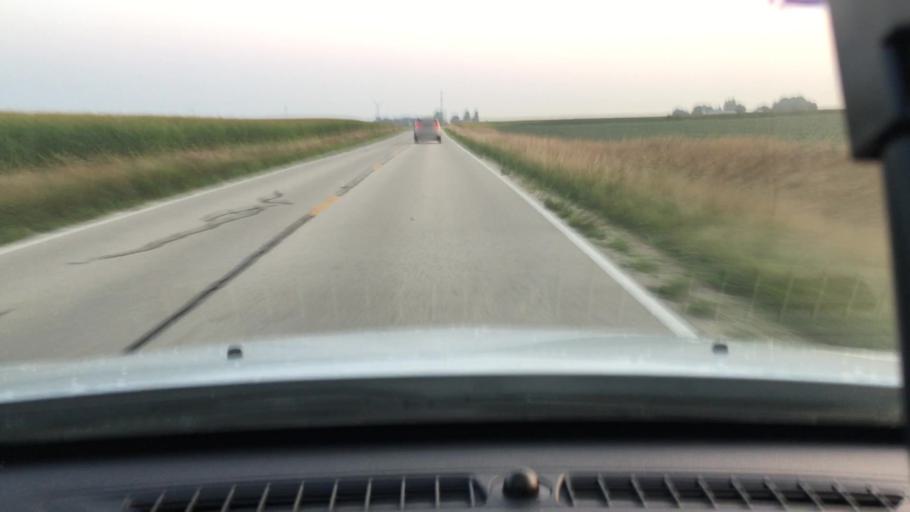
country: US
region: Illinois
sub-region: DeKalb County
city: Malta
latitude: 41.8534
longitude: -88.8480
